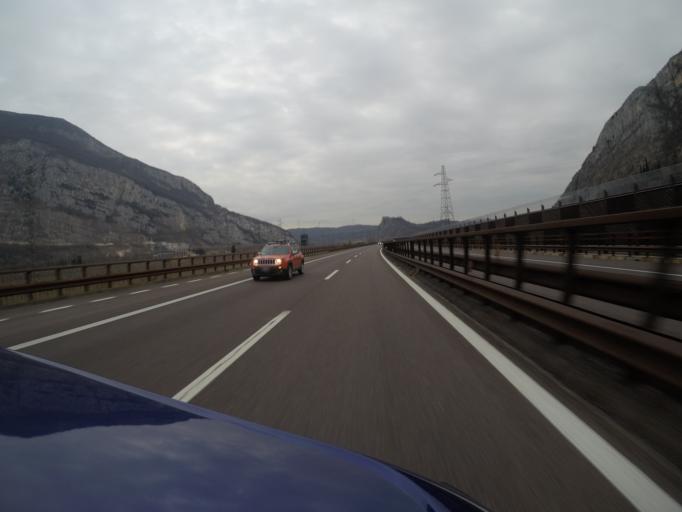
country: IT
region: Veneto
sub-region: Provincia di Verona
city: Dolce
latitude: 45.5875
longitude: 10.8340
